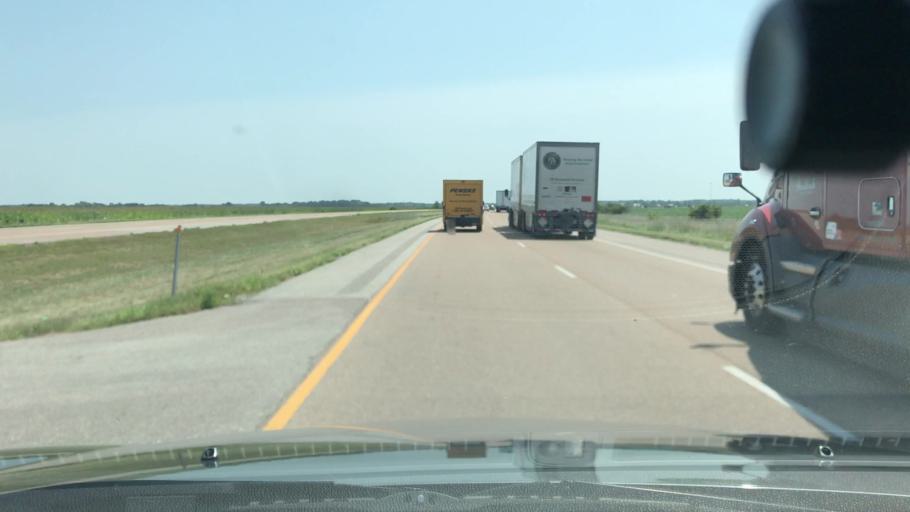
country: US
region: Illinois
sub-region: Washington County
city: Okawville
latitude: 38.4272
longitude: -89.4686
